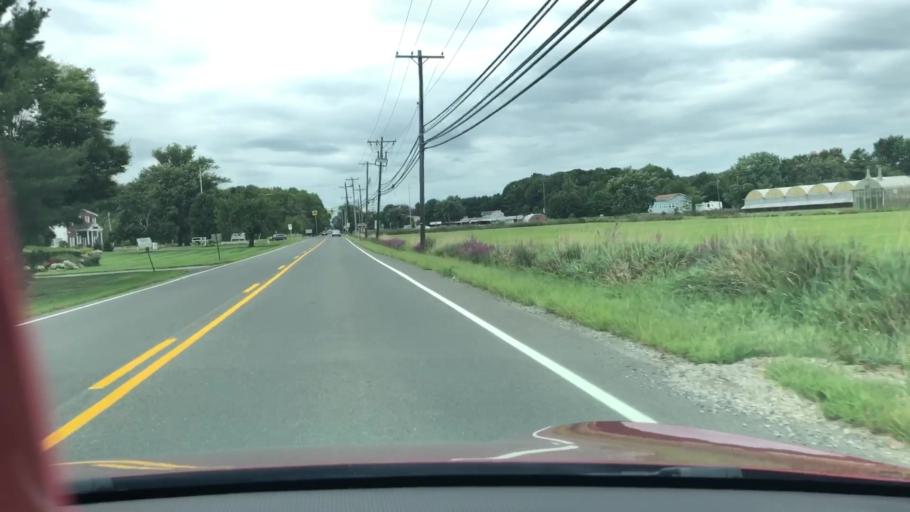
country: US
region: New Jersey
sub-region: Monmouth County
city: Shrewsbury
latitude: 40.1710
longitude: -74.5393
